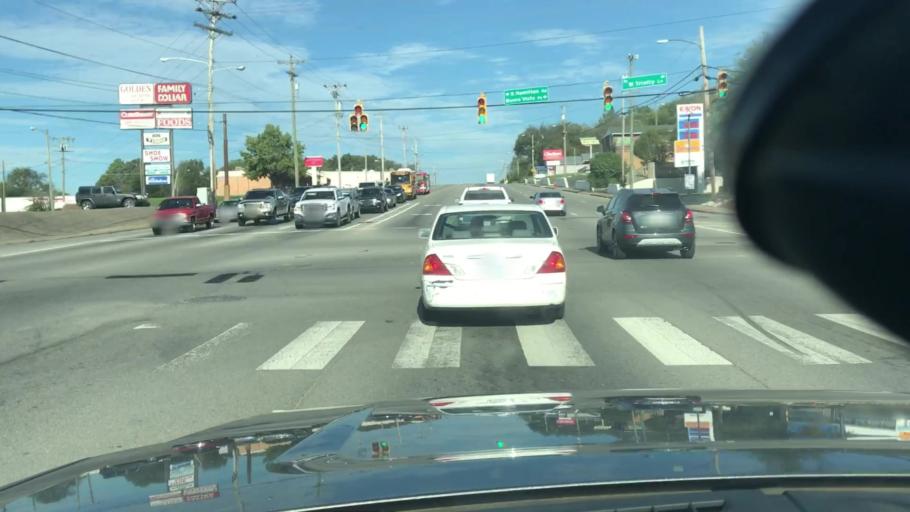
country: US
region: Tennessee
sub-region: Davidson County
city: Nashville
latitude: 36.1936
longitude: -86.8311
